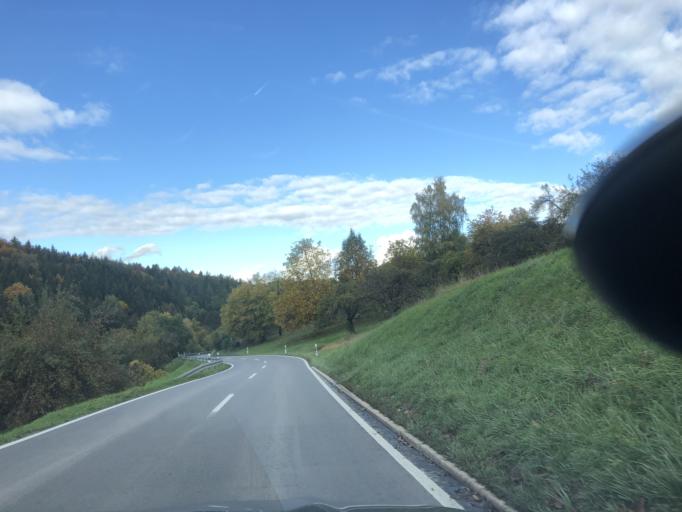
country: DE
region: Baden-Wuerttemberg
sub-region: Regierungsbezirk Stuttgart
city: Winterbach
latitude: 48.8318
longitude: 9.4537
